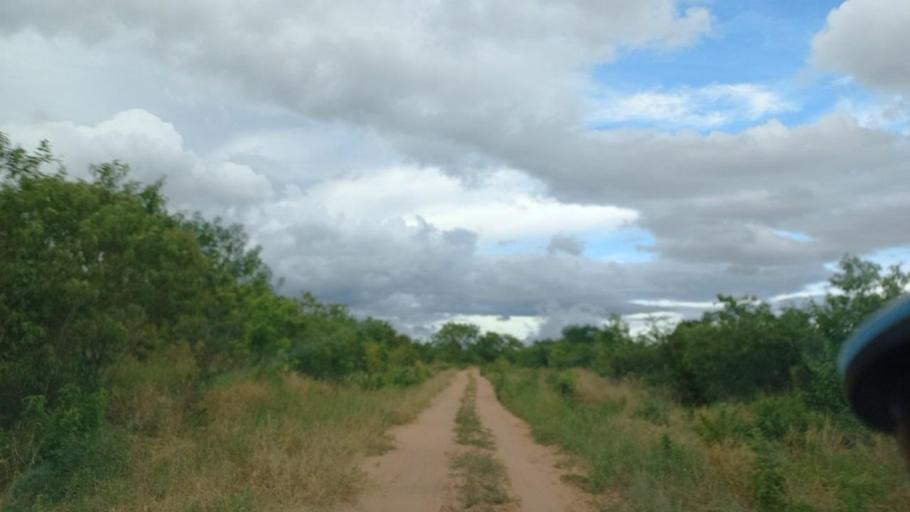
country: ZM
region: Lusaka
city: Luangwa
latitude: -15.5639
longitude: 30.3465
